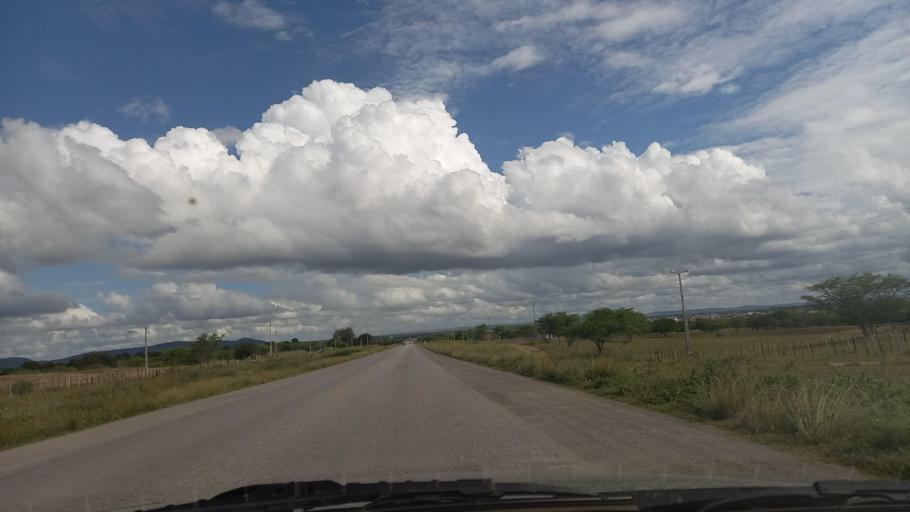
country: BR
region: Pernambuco
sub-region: Cachoeirinha
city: Cachoeirinha
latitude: -8.4702
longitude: -36.2196
